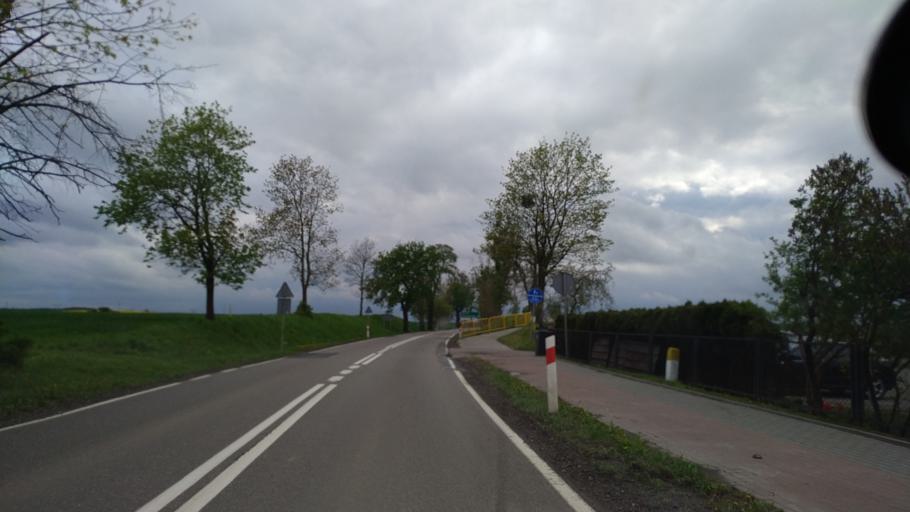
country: PL
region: Pomeranian Voivodeship
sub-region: Powiat kwidzynski
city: Kwidzyn
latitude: 53.7793
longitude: 18.9578
